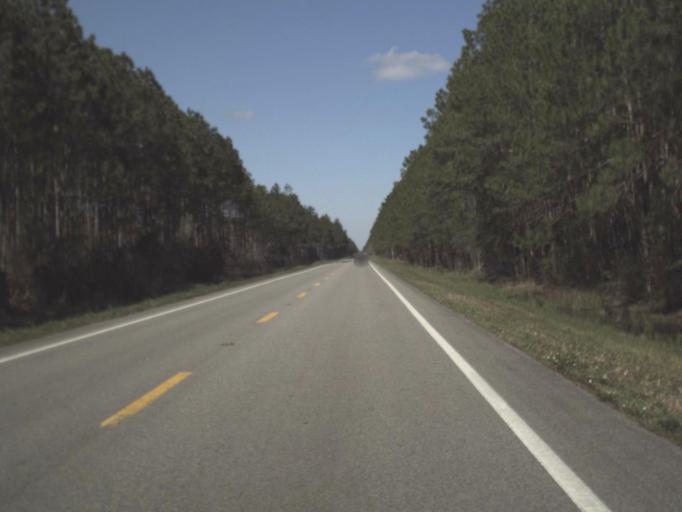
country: US
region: Florida
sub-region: Gulf County
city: Port Saint Joe
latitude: 29.9295
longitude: -85.1939
